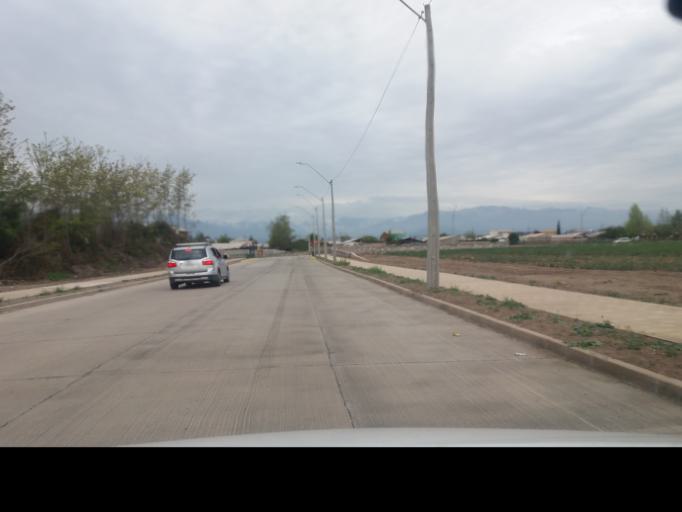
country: CL
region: Valparaiso
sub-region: Provincia de San Felipe
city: San Felipe
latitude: -32.7563
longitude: -70.7151
